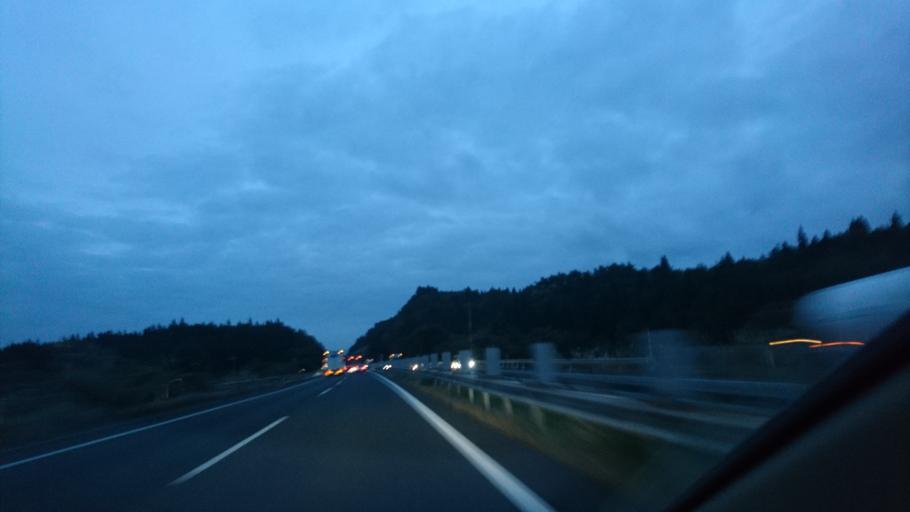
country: JP
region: Iwate
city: Hanamaki
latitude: 39.5015
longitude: 141.1037
